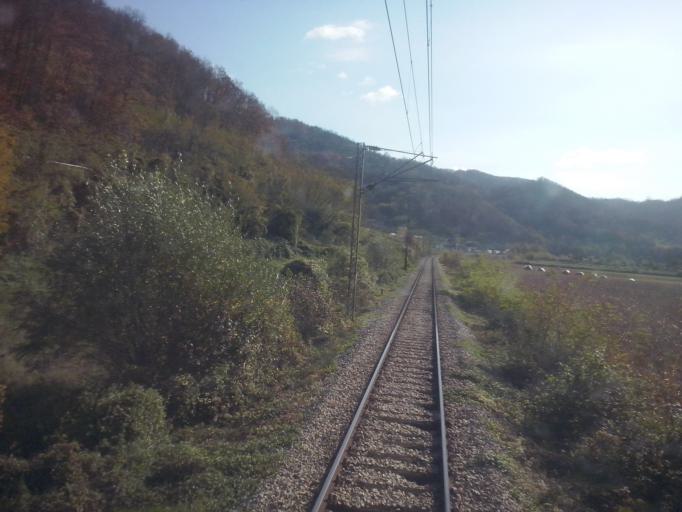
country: RS
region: Central Serbia
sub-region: Zlatiborski Okrug
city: Pozega
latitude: 43.9129
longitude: 19.9970
